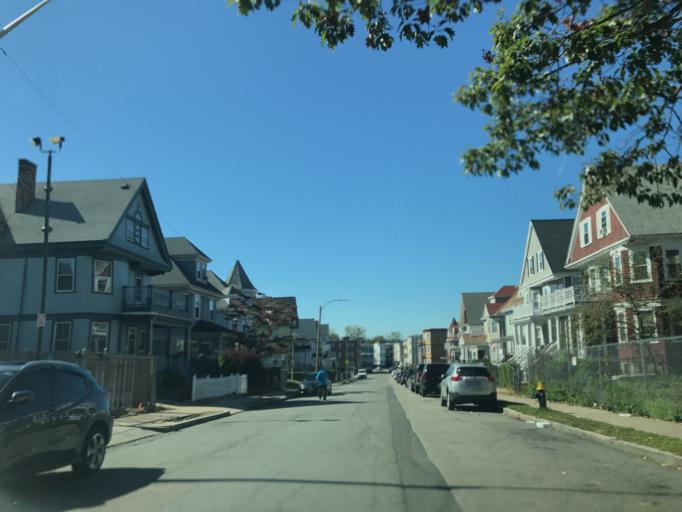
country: US
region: Massachusetts
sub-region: Norfolk County
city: Milton
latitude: 42.2919
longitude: -71.0722
